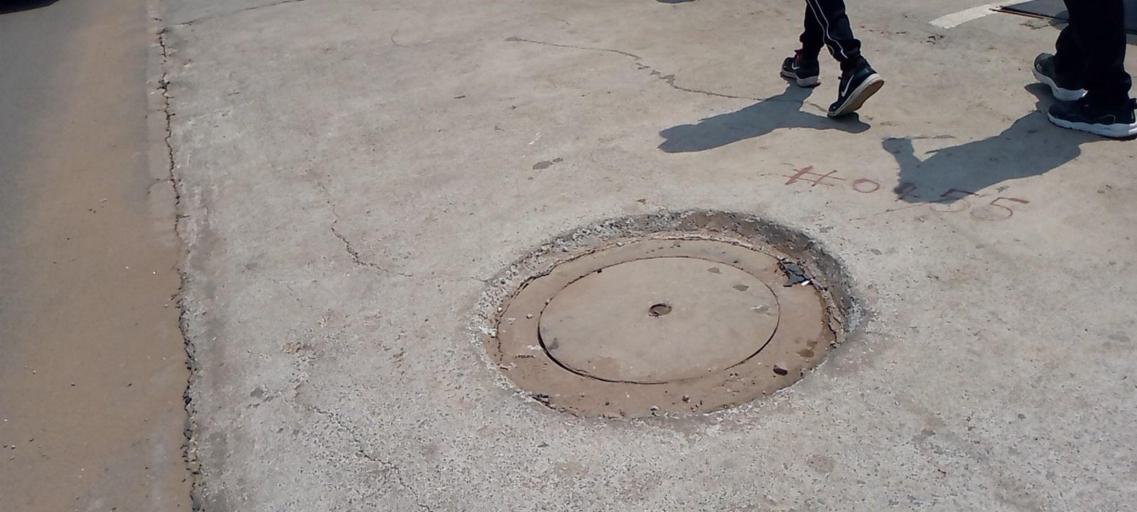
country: ZM
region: Lusaka
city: Lusaka
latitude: -15.4071
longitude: 28.3509
